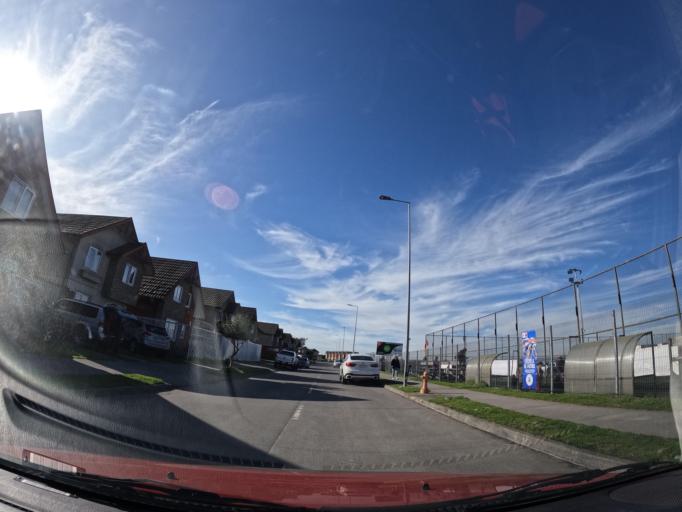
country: CL
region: Biobio
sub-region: Provincia de Concepcion
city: Concepcion
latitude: -36.7706
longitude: -73.0658
